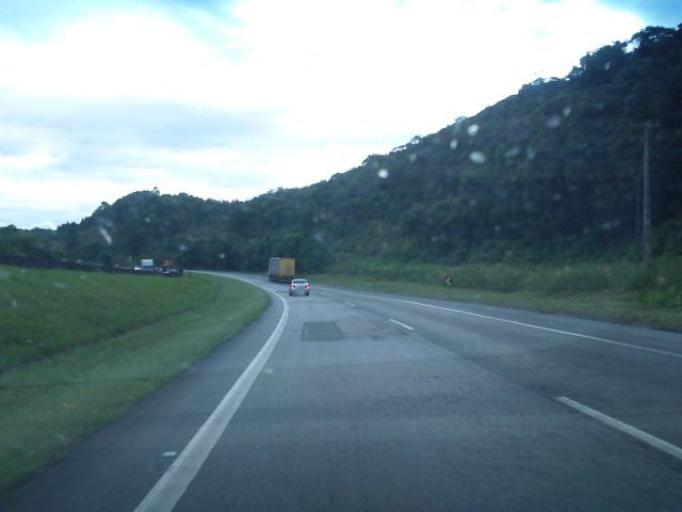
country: BR
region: Parana
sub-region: Campina Grande Do Sul
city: Campina Grande do Sul
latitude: -25.2487
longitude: -48.9079
